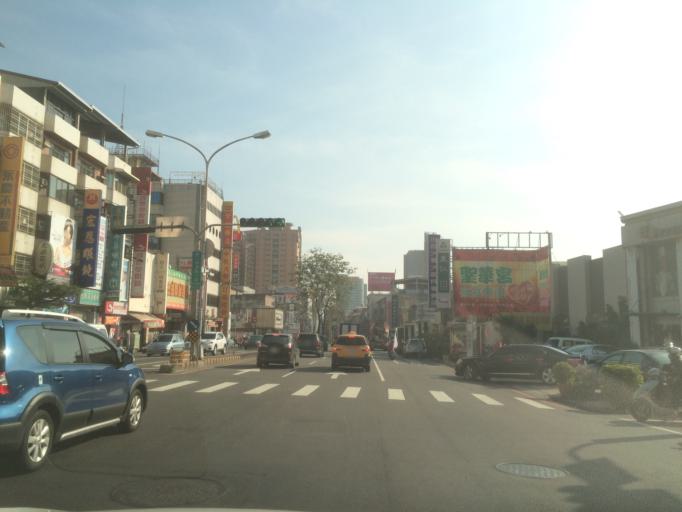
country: TW
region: Taiwan
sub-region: Taichung City
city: Taichung
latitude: 24.1718
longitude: 120.6718
